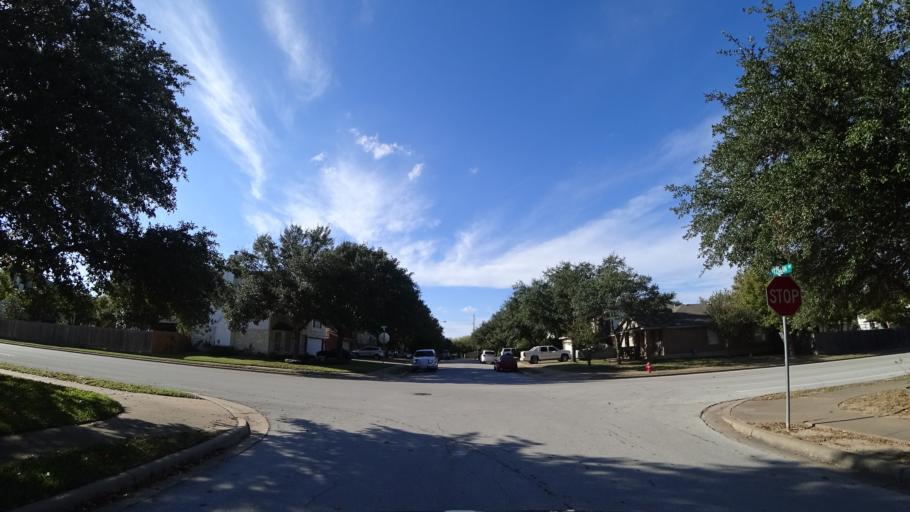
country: US
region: Texas
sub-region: Travis County
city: Wells Branch
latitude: 30.4599
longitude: -97.6884
